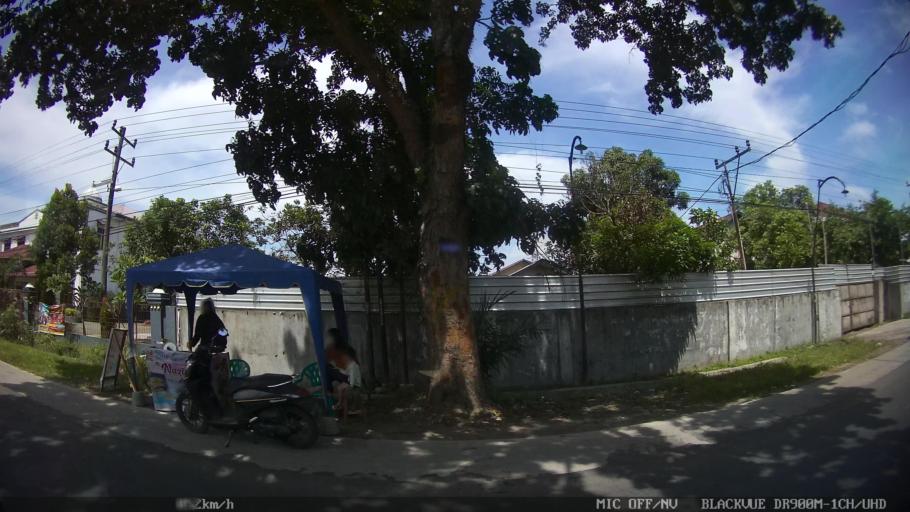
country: ID
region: North Sumatra
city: Binjai
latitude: 3.6477
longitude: 98.5102
